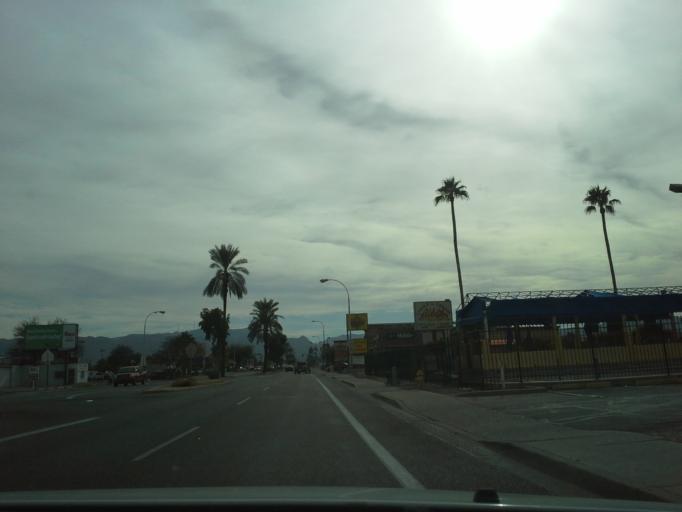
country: US
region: Arizona
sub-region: Maricopa County
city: Phoenix
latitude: 33.3949
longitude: -112.0734
